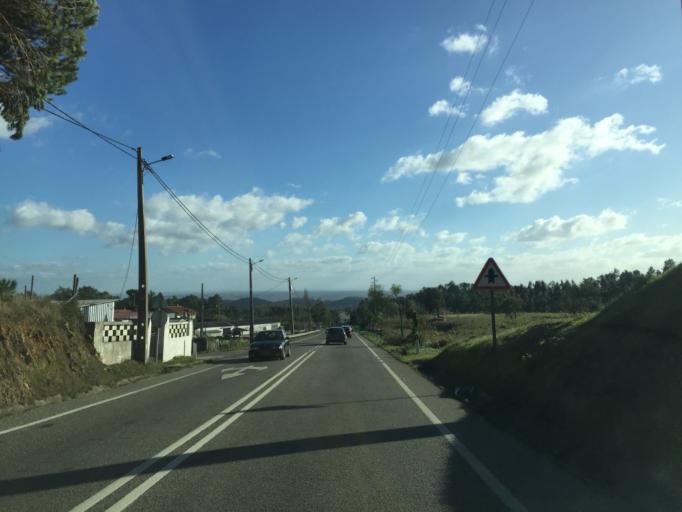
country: PT
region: Coimbra
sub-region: Figueira da Foz
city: Tavarede
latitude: 40.1886
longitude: -8.8301
